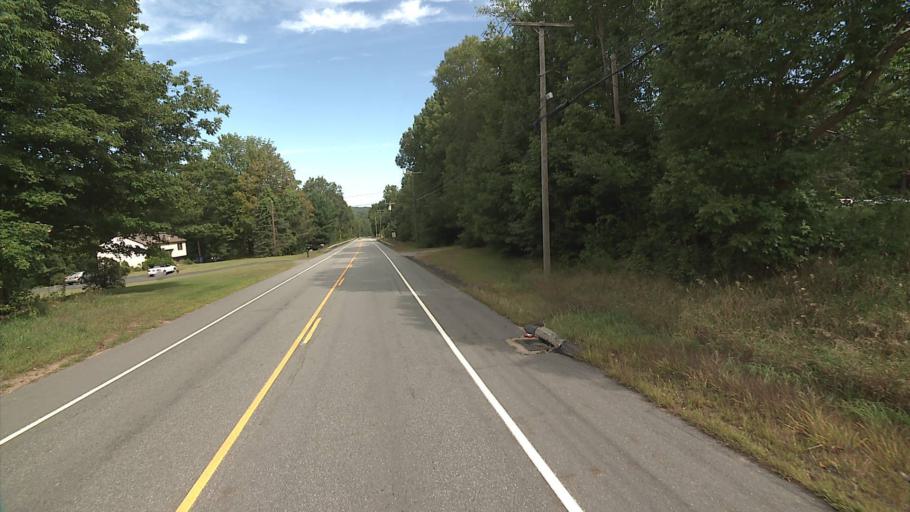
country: US
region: Connecticut
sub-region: Tolland County
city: South Coventry
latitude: 41.8183
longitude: -72.3099
